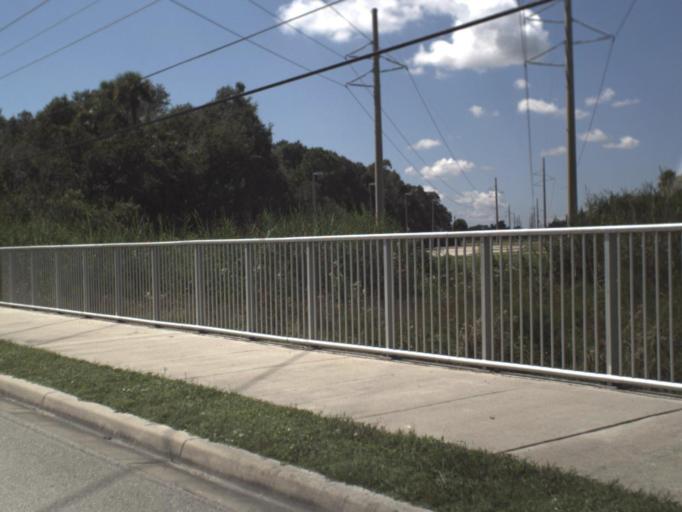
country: US
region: Florida
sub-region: Lee County
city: Suncoast Estates
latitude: 26.7094
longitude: -81.8389
